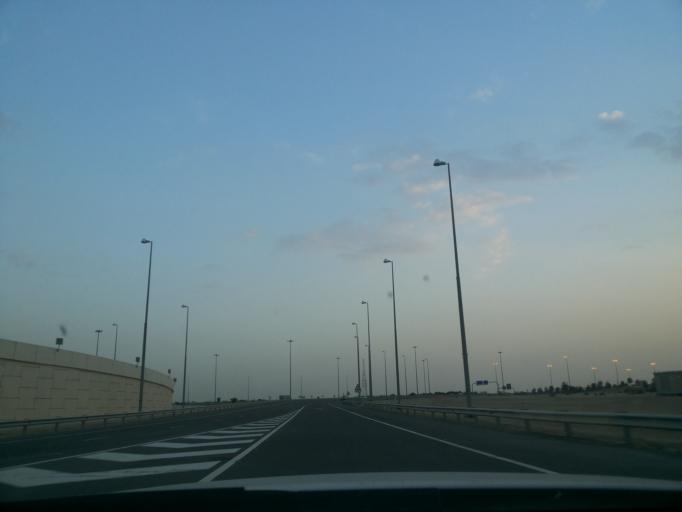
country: AE
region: Abu Dhabi
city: Abu Dhabi
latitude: 24.6943
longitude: 54.7761
